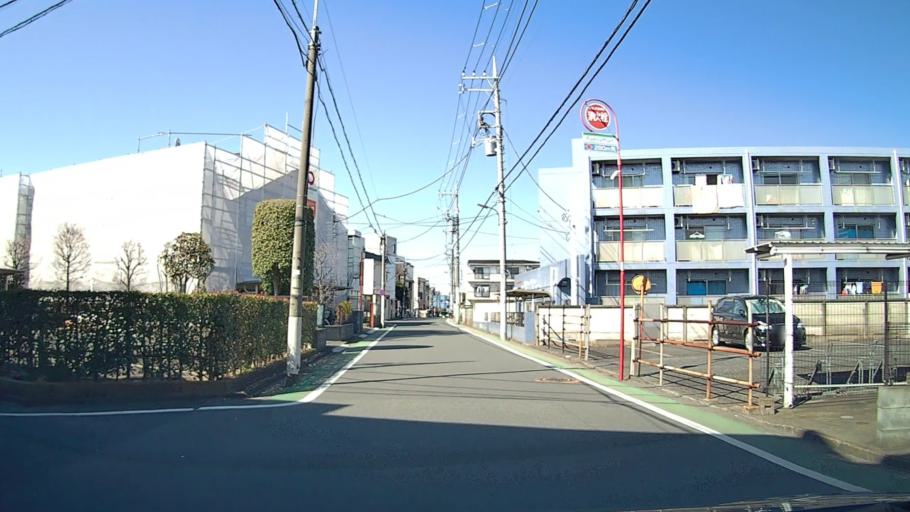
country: JP
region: Saitama
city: Wako
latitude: 35.7456
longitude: 139.6007
